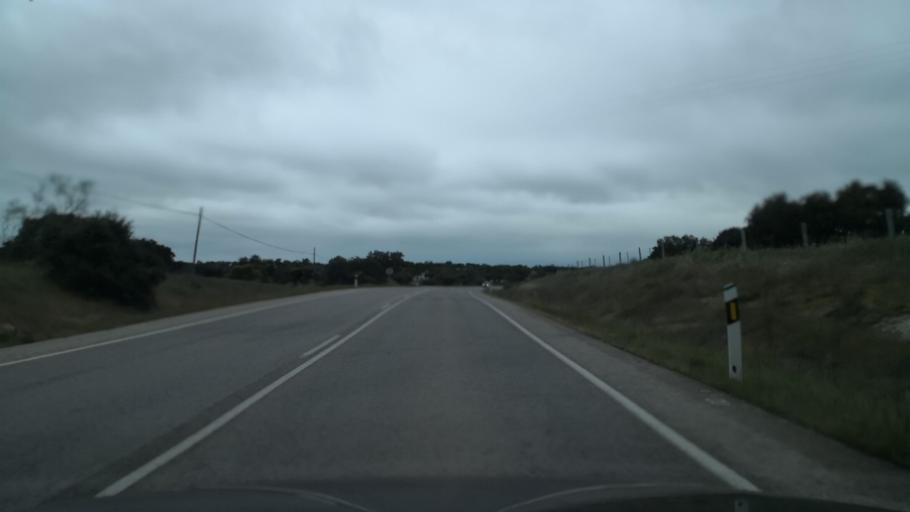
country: ES
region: Extremadura
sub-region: Provincia de Caceres
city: Caceres
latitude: 39.4007
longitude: -6.4216
